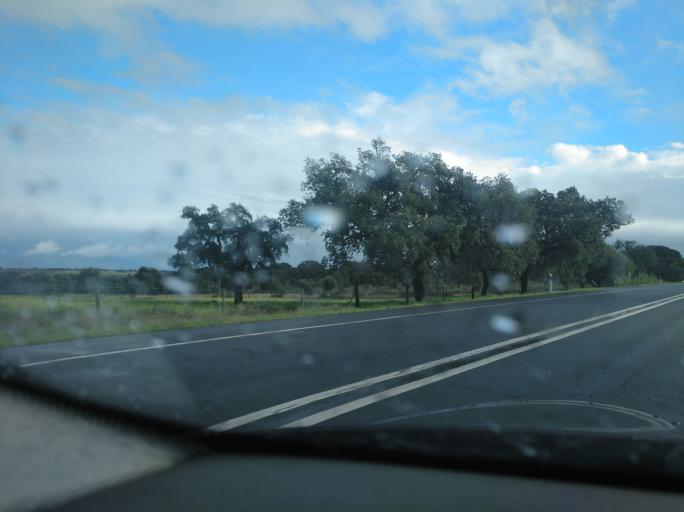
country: PT
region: Setubal
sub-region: Grandola
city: Grandola
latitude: 38.0555
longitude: -8.4037
